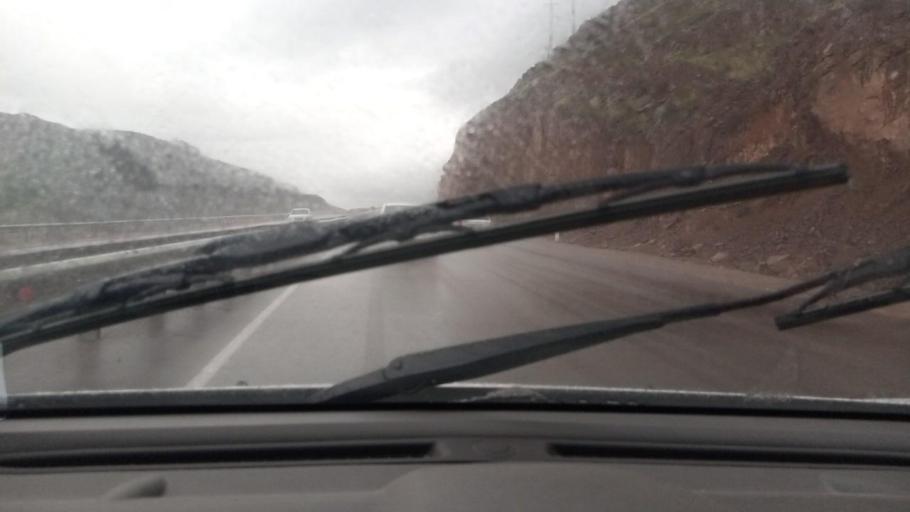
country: UZ
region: Toshkent
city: Angren
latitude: 41.0738
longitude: 70.2826
